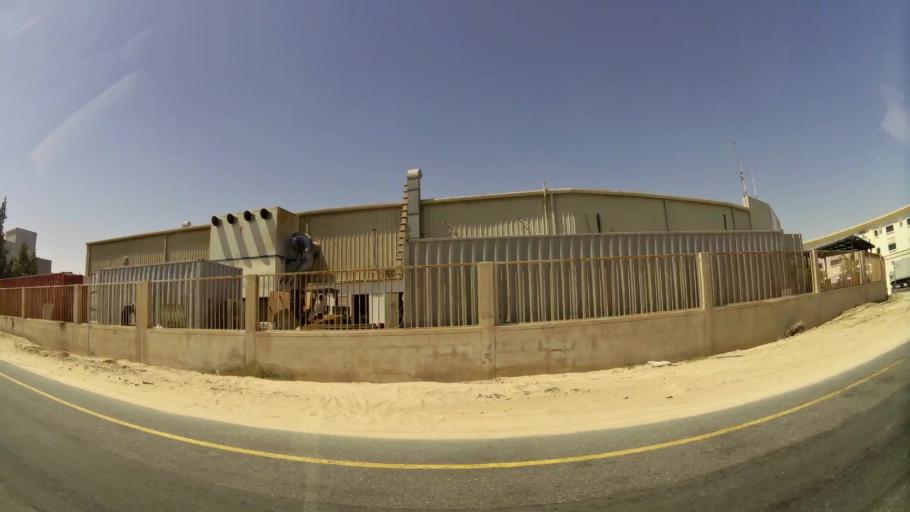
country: AE
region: Dubai
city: Dubai
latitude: 24.9879
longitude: 55.2078
